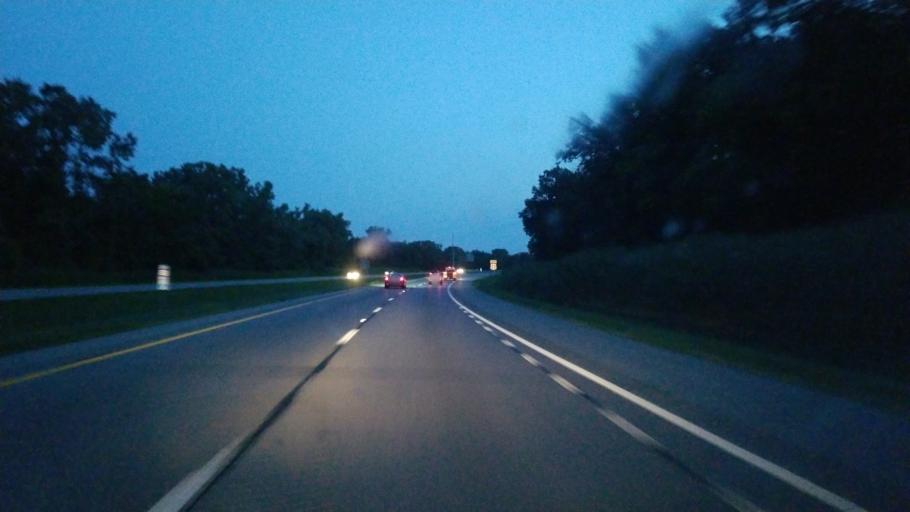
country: US
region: Ohio
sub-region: Lucas County
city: Sylvania
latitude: 41.7086
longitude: -83.6887
